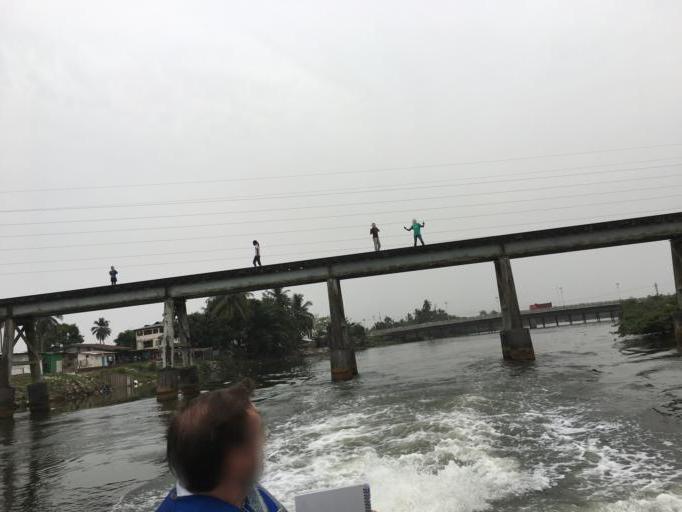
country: LR
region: Montserrado
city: Monrovia
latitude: 6.3710
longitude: -10.7784
